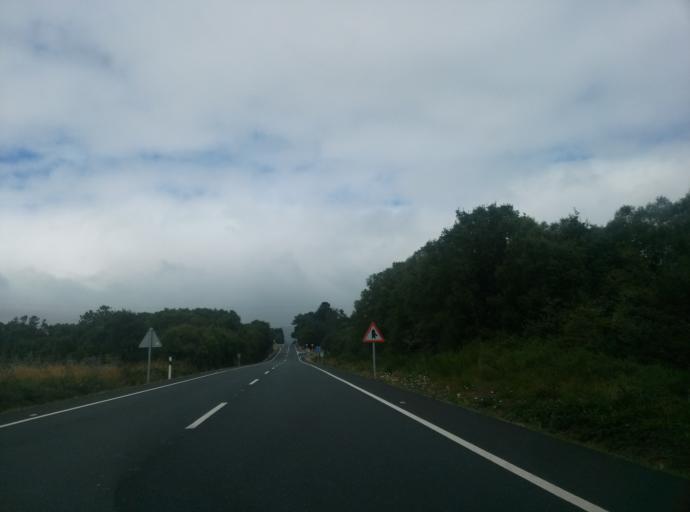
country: ES
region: Galicia
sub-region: Provincia de Lugo
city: Muras
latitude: 43.4040
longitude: -7.7802
